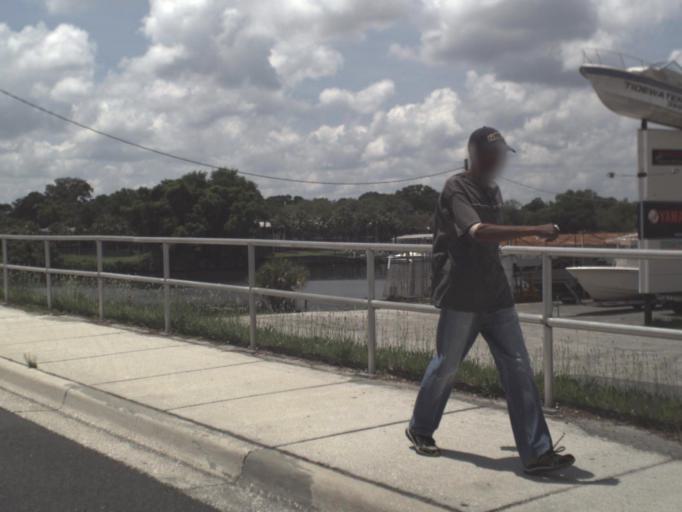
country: US
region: Florida
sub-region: Duval County
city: Jacksonville
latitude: 30.2743
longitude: -81.7323
